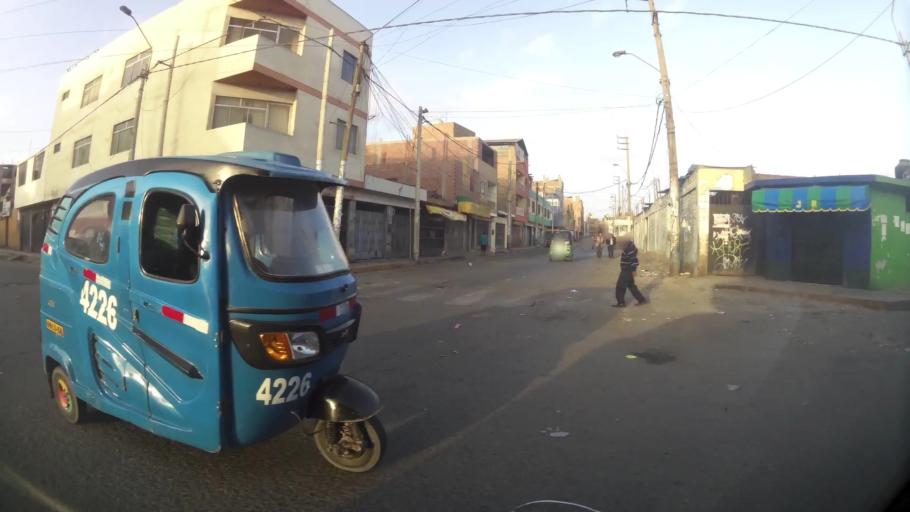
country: PE
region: Lima
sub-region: Huaura
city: Huacho
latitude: -11.1031
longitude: -77.6090
